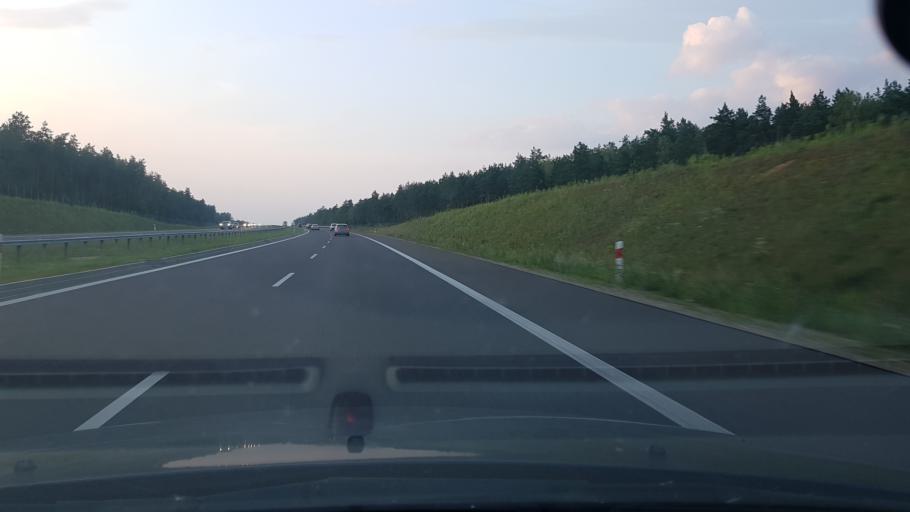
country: PL
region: Masovian Voivodeship
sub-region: Powiat mlawski
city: Wieczfnia Koscielna
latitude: 53.2411
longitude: 20.4241
